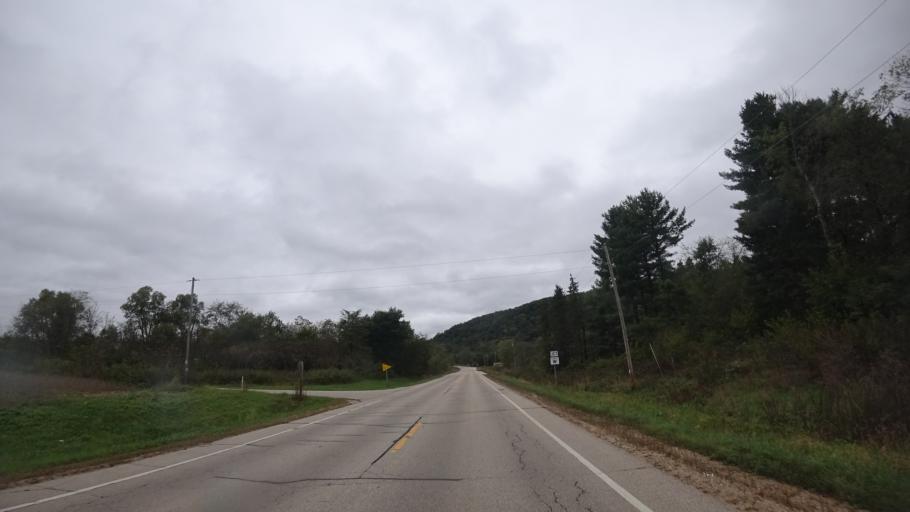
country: US
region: Wisconsin
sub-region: Grant County
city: Boscobel
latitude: 43.2053
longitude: -90.6367
